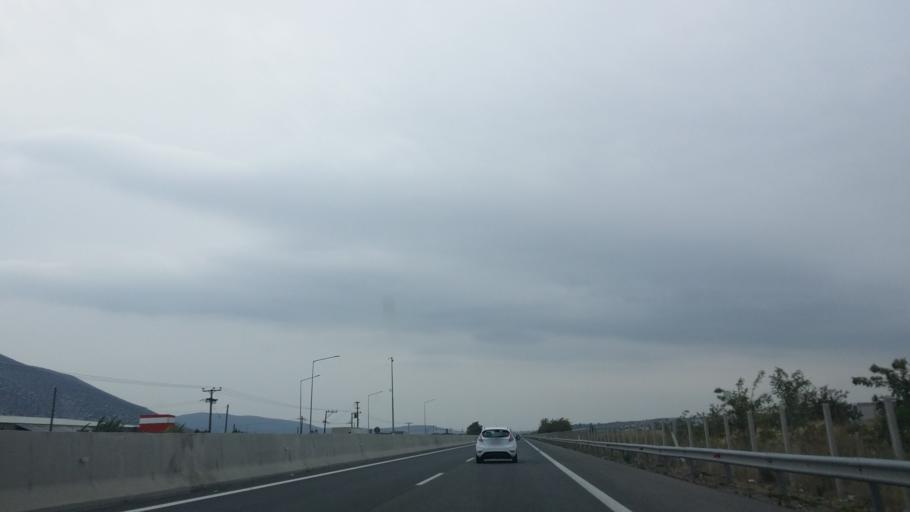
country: GR
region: Central Greece
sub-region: Nomos Voiotias
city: Thivai
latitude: 38.3713
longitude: 23.3938
